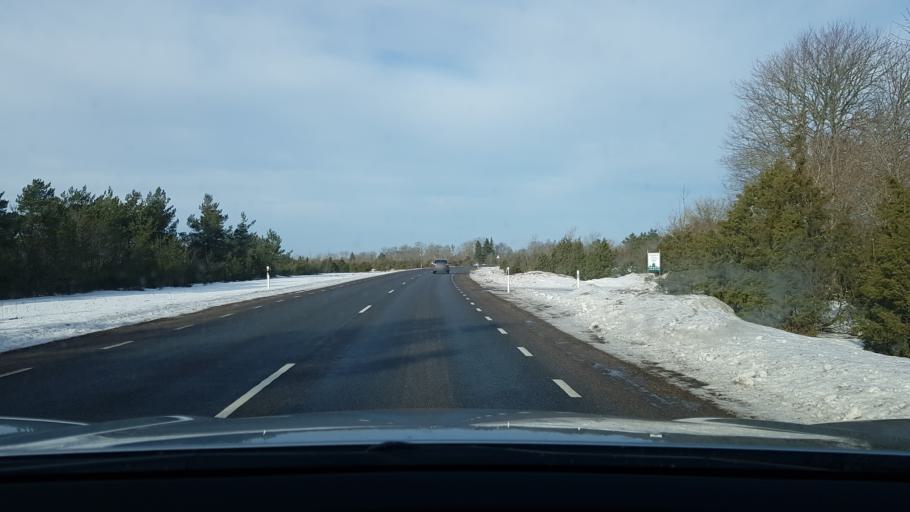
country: EE
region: Saare
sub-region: Kuressaare linn
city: Kuressaare
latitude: 58.2860
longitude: 22.5402
